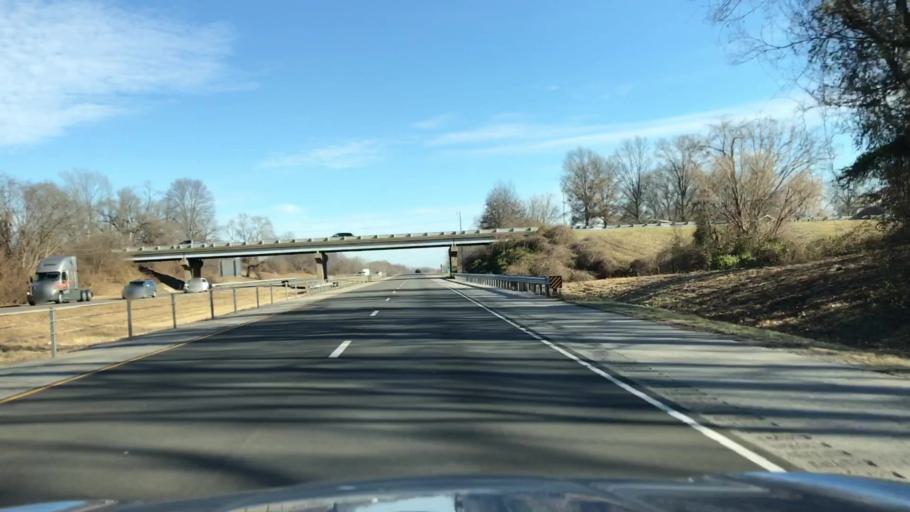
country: US
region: Illinois
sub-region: Madison County
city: Glen Carbon
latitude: 38.7567
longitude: -89.9762
